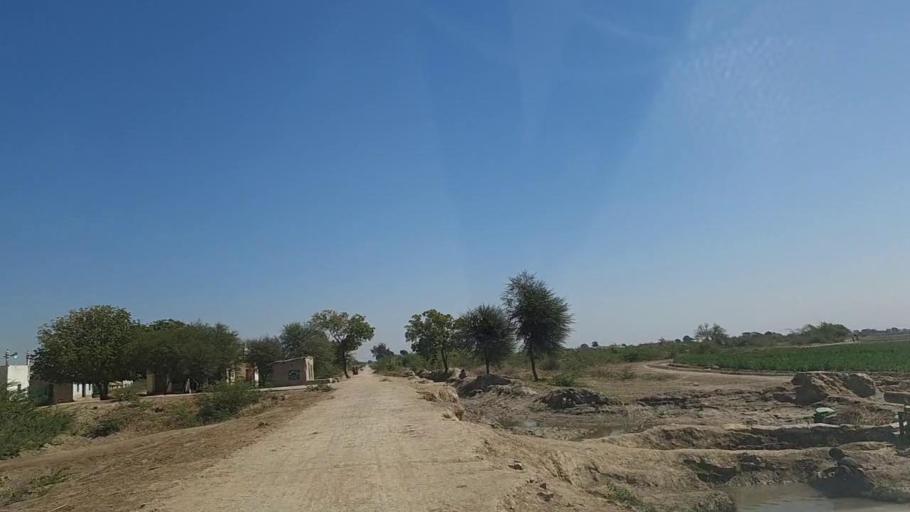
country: PK
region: Sindh
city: Samaro
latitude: 25.3467
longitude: 69.4857
